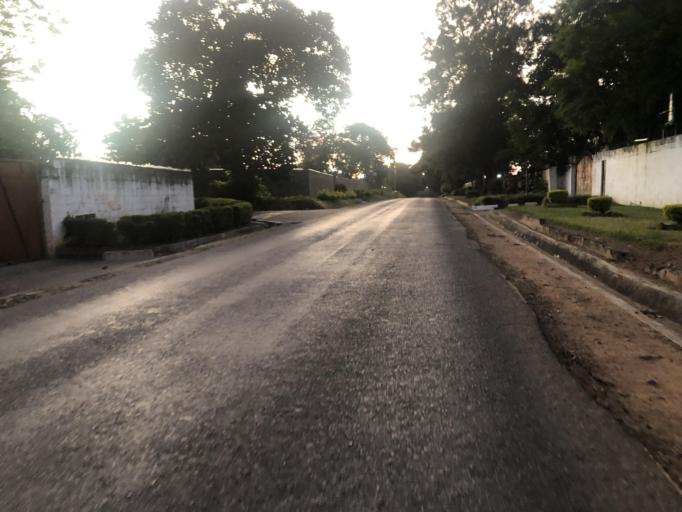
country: ZM
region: Lusaka
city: Lusaka
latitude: -15.3892
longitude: 28.3385
